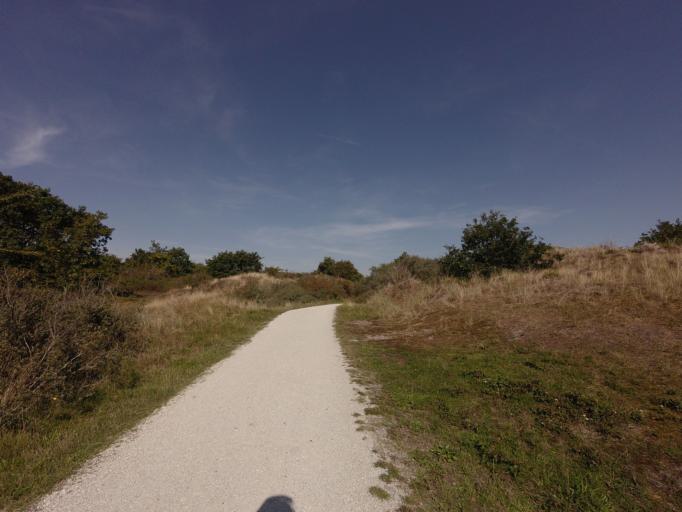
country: NL
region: Friesland
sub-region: Gemeente Schiermonnikoog
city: Schiermonnikoog
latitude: 53.4789
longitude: 6.1443
